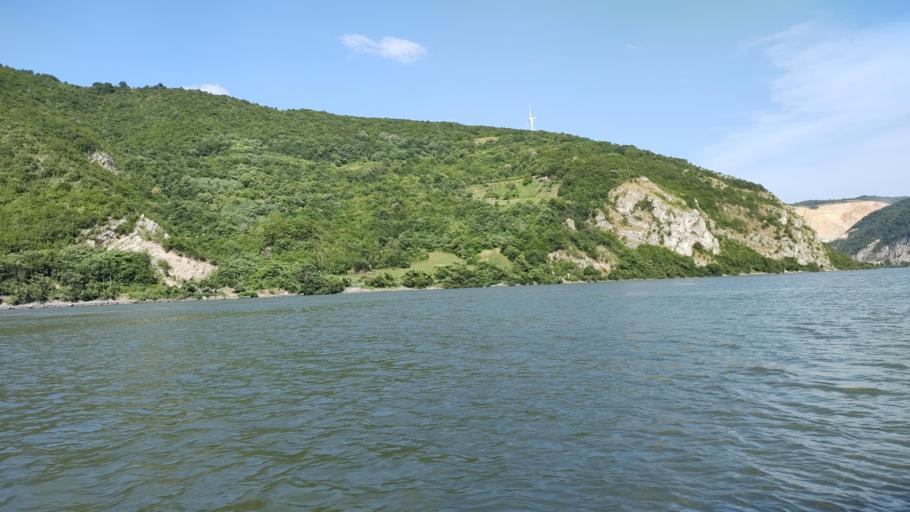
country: RO
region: Caras-Severin
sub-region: Comuna Pescari
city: Coronini
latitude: 44.6603
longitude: 21.7034
